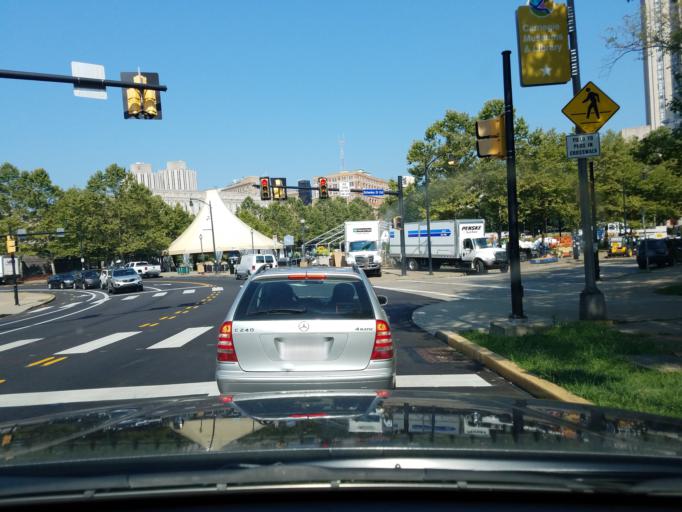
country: US
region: Pennsylvania
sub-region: Allegheny County
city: Bloomfield
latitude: 40.4424
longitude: -79.9514
